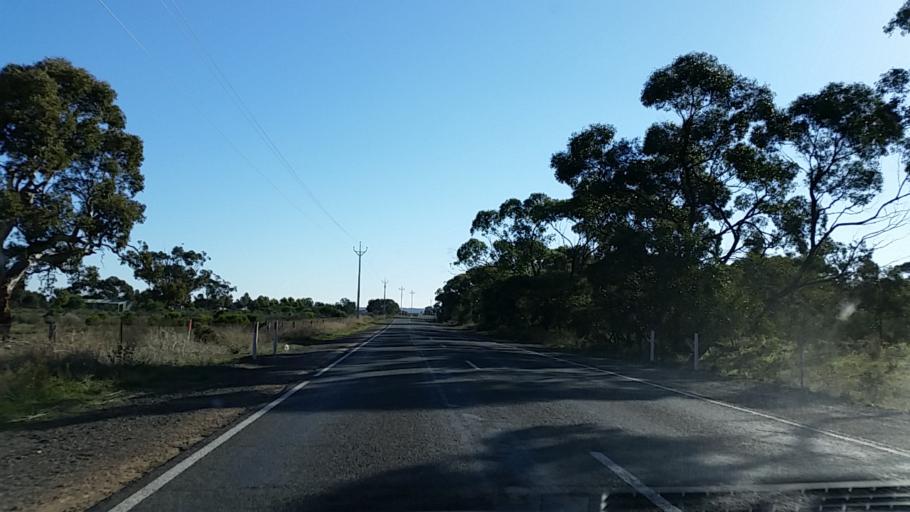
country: AU
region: South Australia
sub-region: Mount Barker
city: Callington
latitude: -35.1186
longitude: 139.1367
